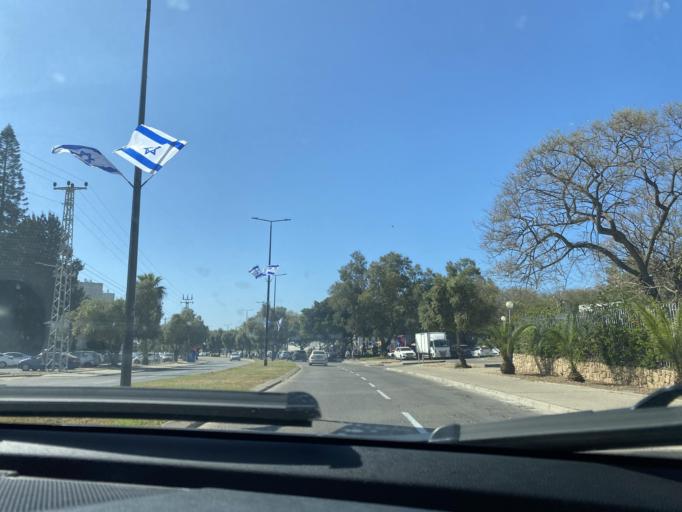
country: IL
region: Southern District
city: Ashqelon
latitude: 31.6829
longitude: 34.5697
